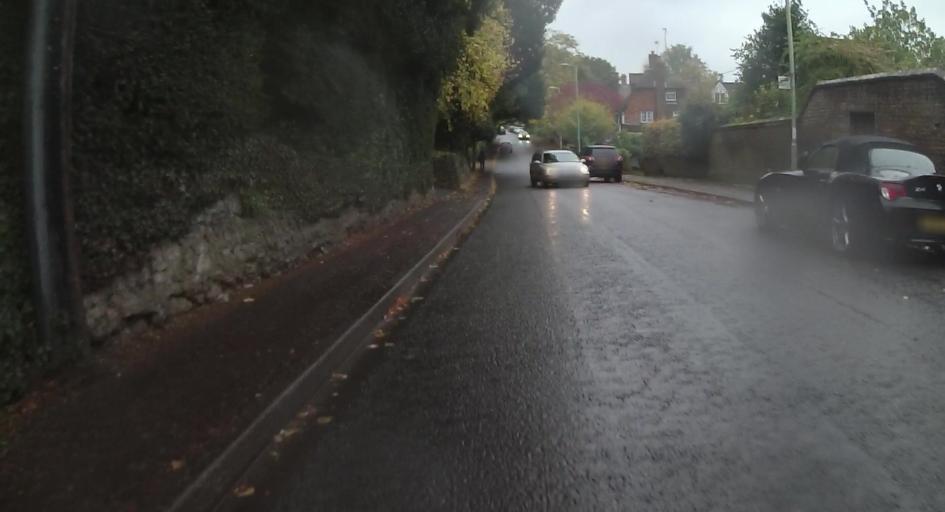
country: GB
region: England
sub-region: Hampshire
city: Alton
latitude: 51.1623
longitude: -0.9518
